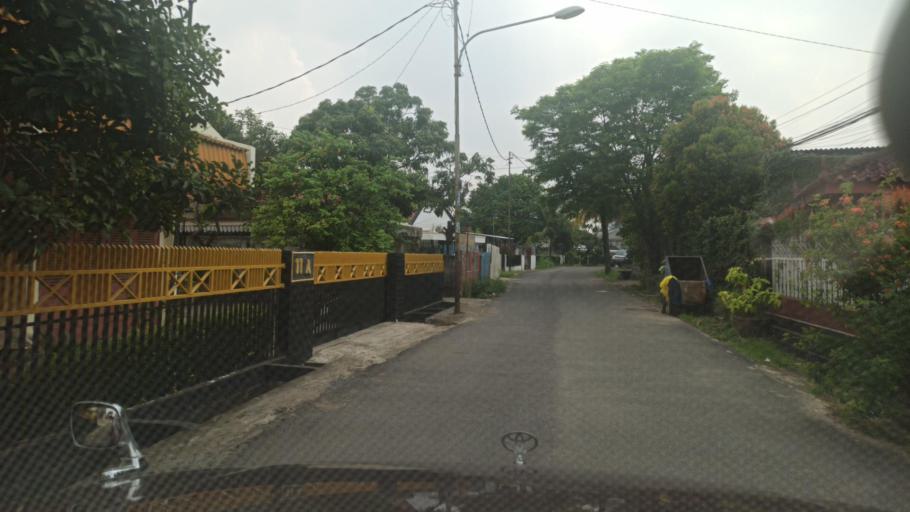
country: ID
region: South Sumatra
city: Plaju
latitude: -2.9922
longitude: 104.7416
